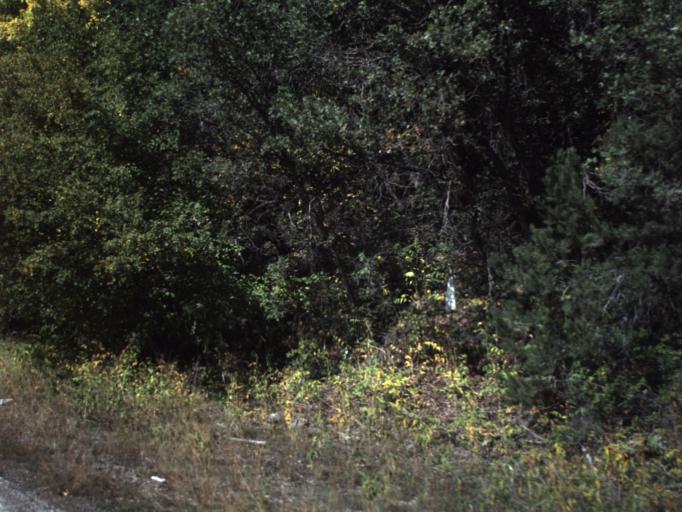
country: US
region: Utah
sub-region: Beaver County
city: Beaver
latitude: 38.2731
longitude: -112.5516
